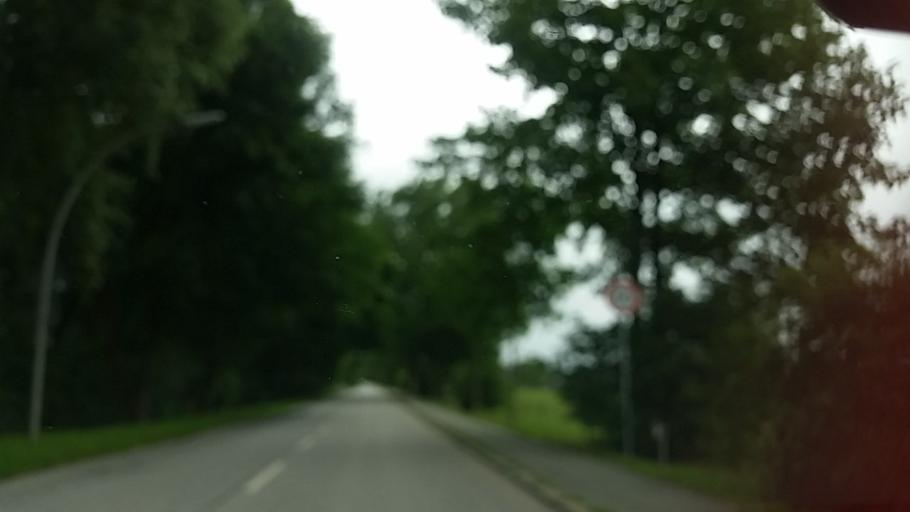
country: DE
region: Schleswig-Holstein
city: Oststeinbek
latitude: 53.4998
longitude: 10.1357
